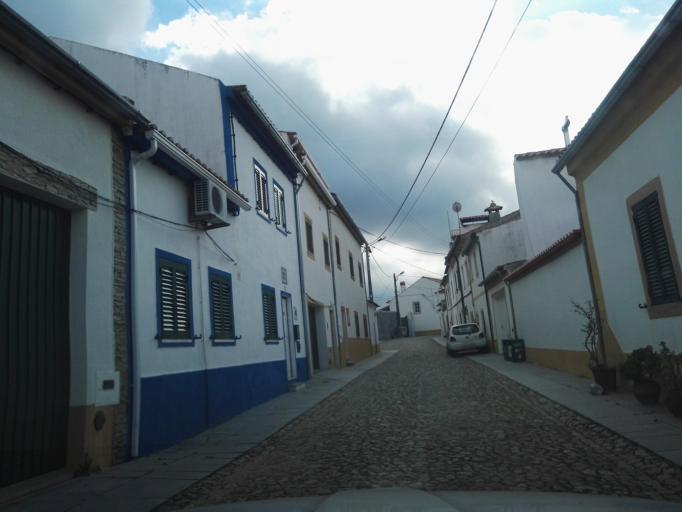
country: PT
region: Portalegre
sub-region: Nisa
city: Nisa
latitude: 39.4845
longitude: -7.7234
